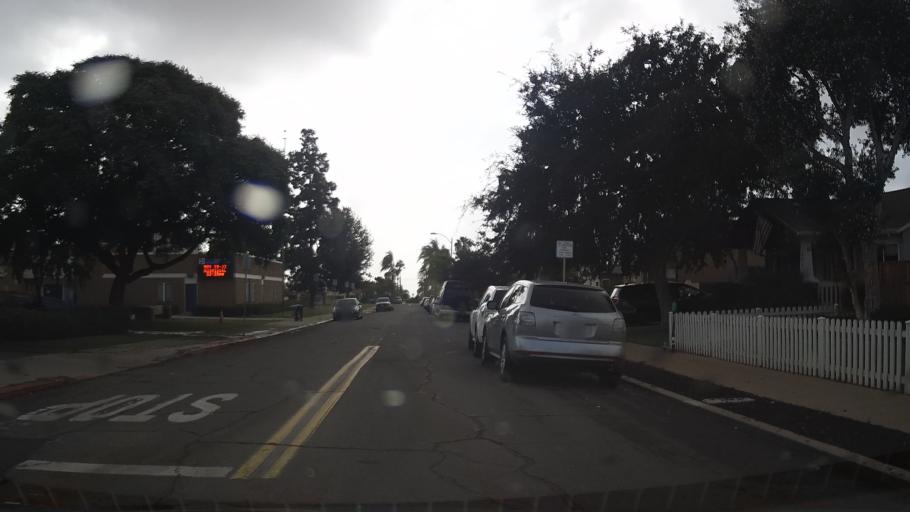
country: US
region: California
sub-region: San Diego County
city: San Diego
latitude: 32.7374
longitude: -117.1222
